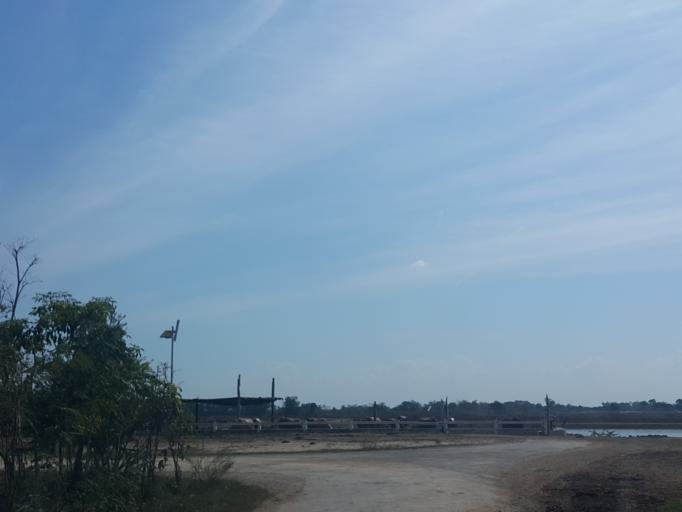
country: TH
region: Sukhothai
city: Si Samrong
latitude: 17.2285
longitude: 99.8210
